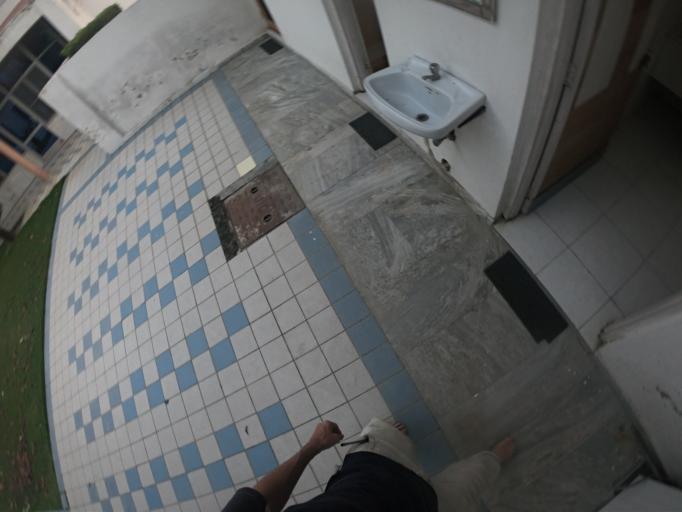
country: IN
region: Punjab
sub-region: Shahid Bhagat Singh Nagar
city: Rahon
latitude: 31.0218
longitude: 76.0920
